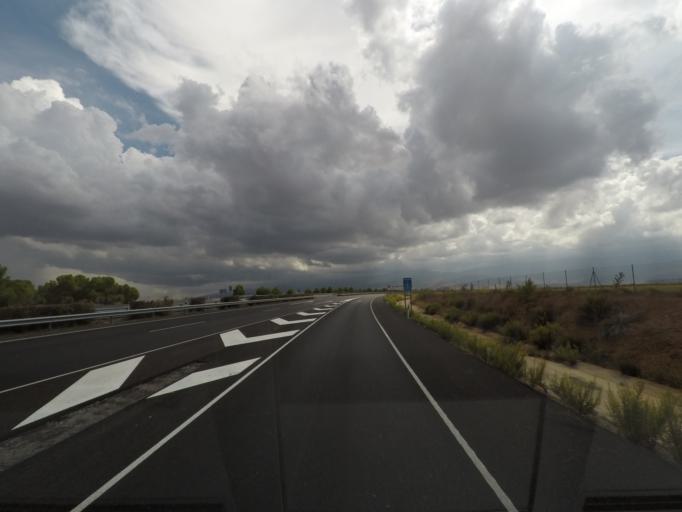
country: ES
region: Andalusia
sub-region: Provincia de Granada
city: Albunan
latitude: 37.2601
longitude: -3.0834
